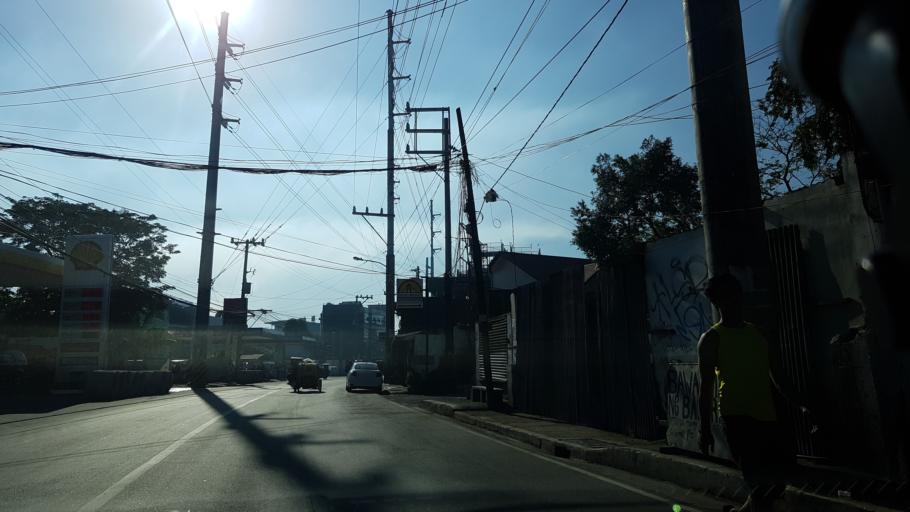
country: PH
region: Calabarzon
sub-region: Province of Rizal
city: Pateros
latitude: 14.5532
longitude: 121.0721
